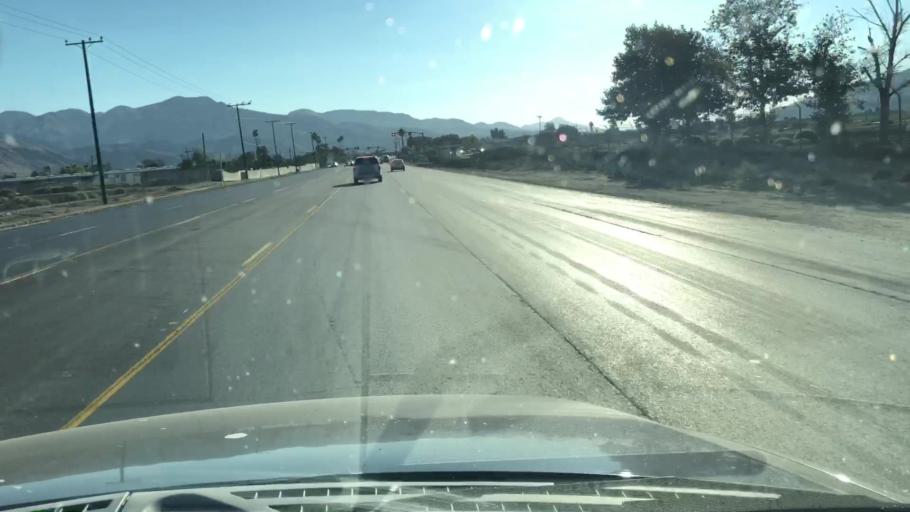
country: US
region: California
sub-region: Ventura County
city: Piru
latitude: 34.4072
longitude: -118.7914
